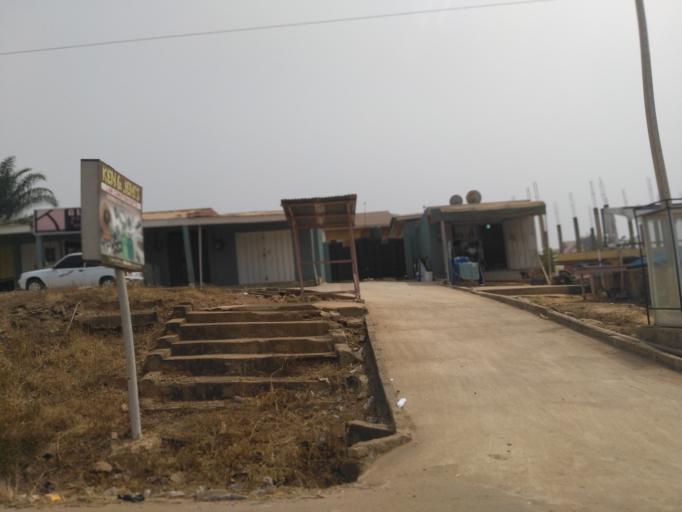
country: GH
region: Ashanti
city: Kumasi
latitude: 6.6482
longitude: -1.6437
